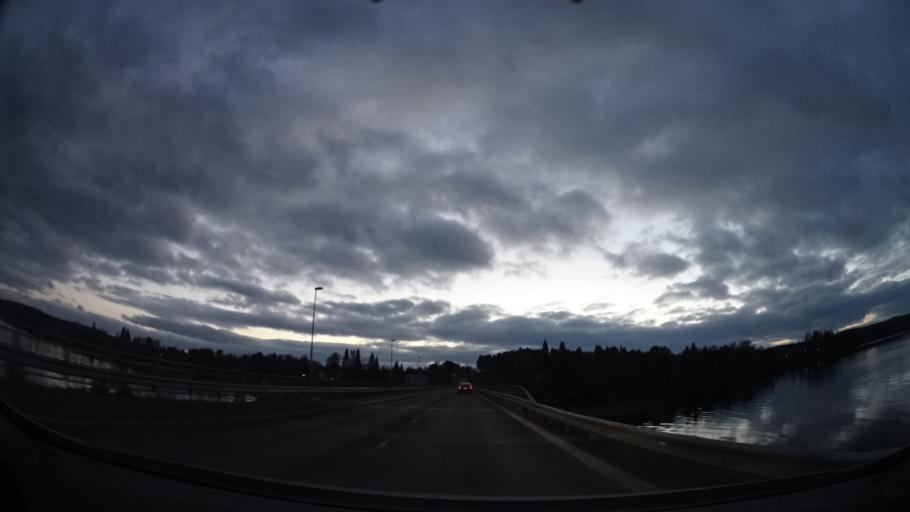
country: SE
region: Vaesterbotten
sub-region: Asele Kommun
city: Asele
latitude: 64.1662
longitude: 17.3654
